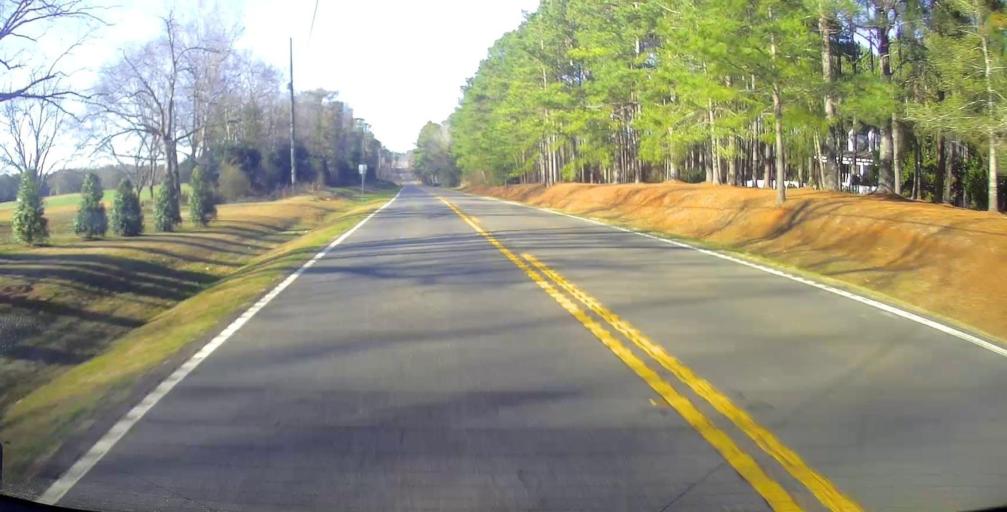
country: US
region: Georgia
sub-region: Sumter County
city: Americus
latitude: 32.0339
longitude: -84.2194
